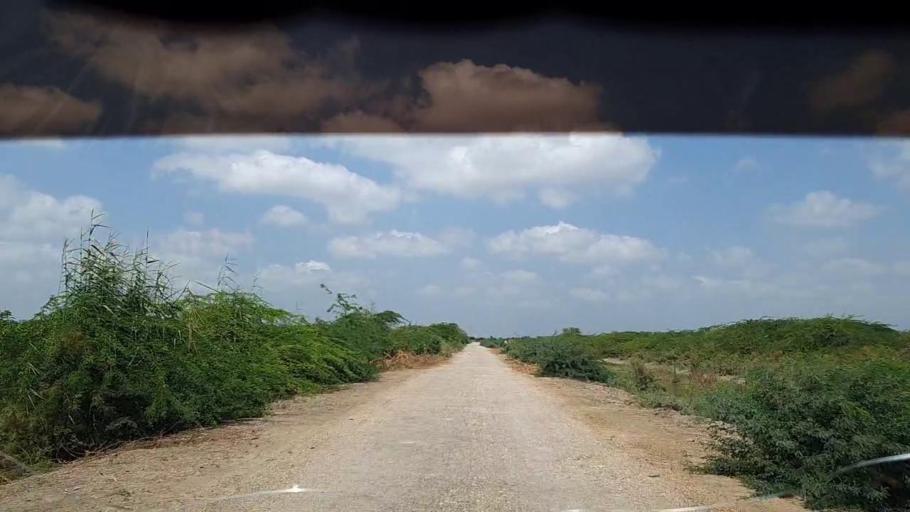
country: PK
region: Sindh
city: Kadhan
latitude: 24.5852
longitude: 68.9700
